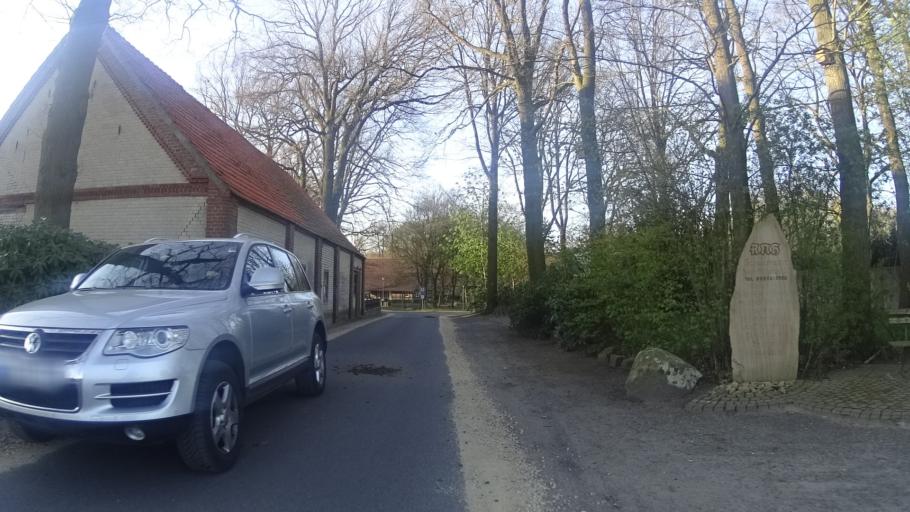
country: DE
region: North Rhine-Westphalia
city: Emsdetten
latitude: 52.2210
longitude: 7.5068
